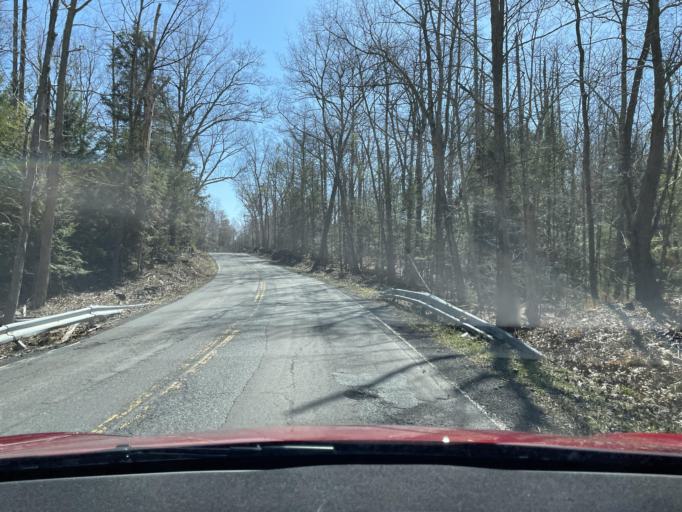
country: US
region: New York
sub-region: Ulster County
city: Lake Katrine
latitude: 42.0451
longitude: -74.0131
